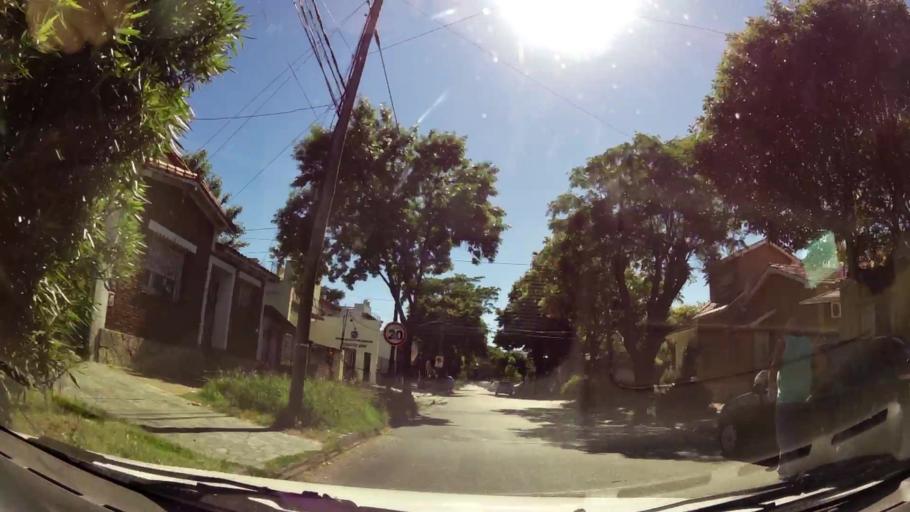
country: AR
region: Buenos Aires
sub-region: Partido de Vicente Lopez
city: Olivos
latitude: -34.5209
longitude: -58.4918
